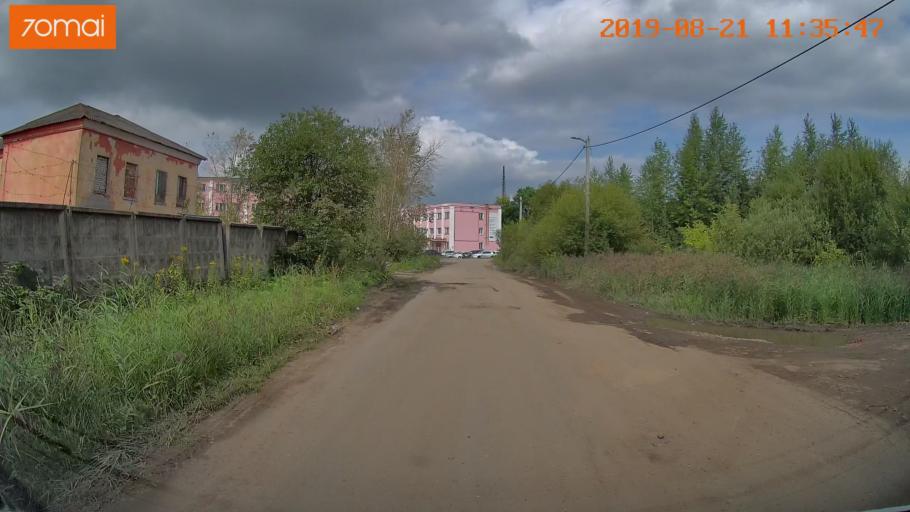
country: RU
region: Ivanovo
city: Novo-Talitsy
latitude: 56.9906
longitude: 40.9096
